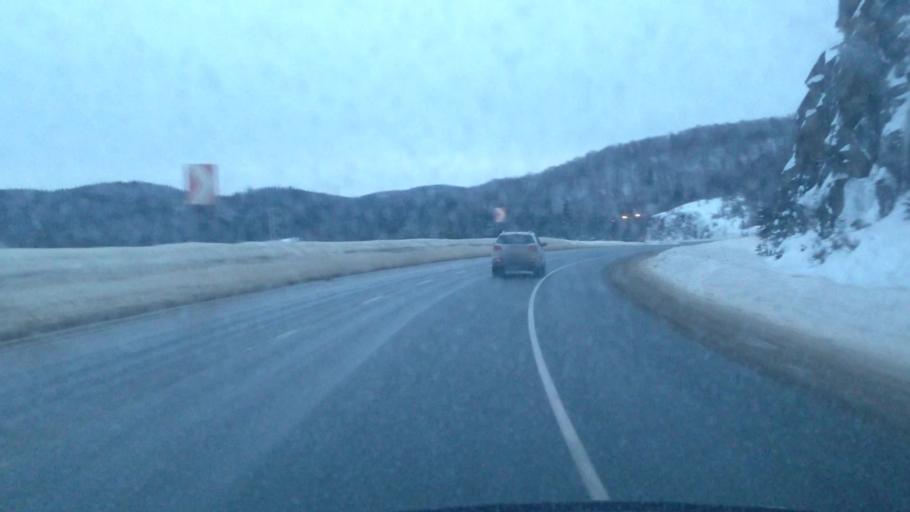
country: CA
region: Quebec
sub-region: Laurentides
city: Sainte-Agathe-des-Monts
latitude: 46.1093
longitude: -74.4186
